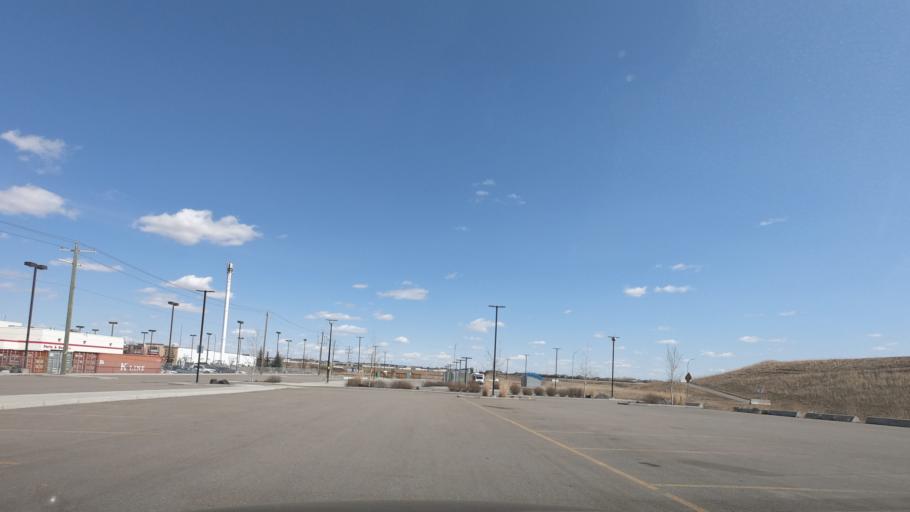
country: CA
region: Alberta
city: Airdrie
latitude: 51.2573
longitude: -114.0074
